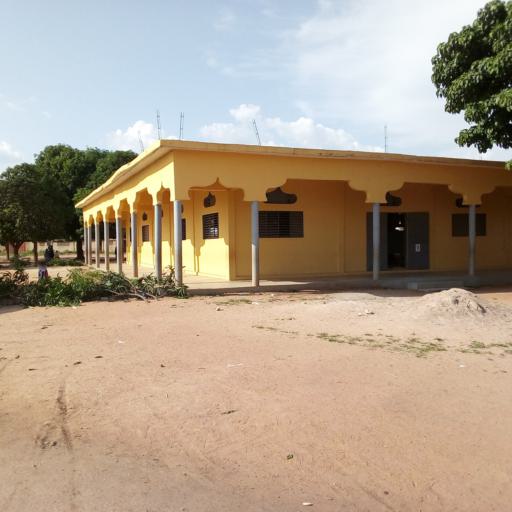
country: CI
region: Vallee du Bandama
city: Bouake
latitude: 7.7260
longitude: -4.9969
